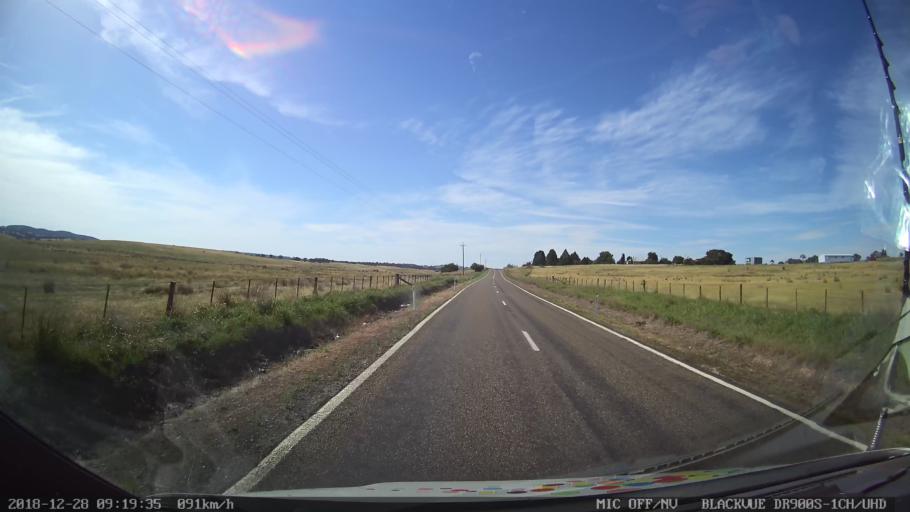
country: AU
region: New South Wales
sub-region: Upper Lachlan Shire
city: Crookwell
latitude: -34.3386
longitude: 149.3694
